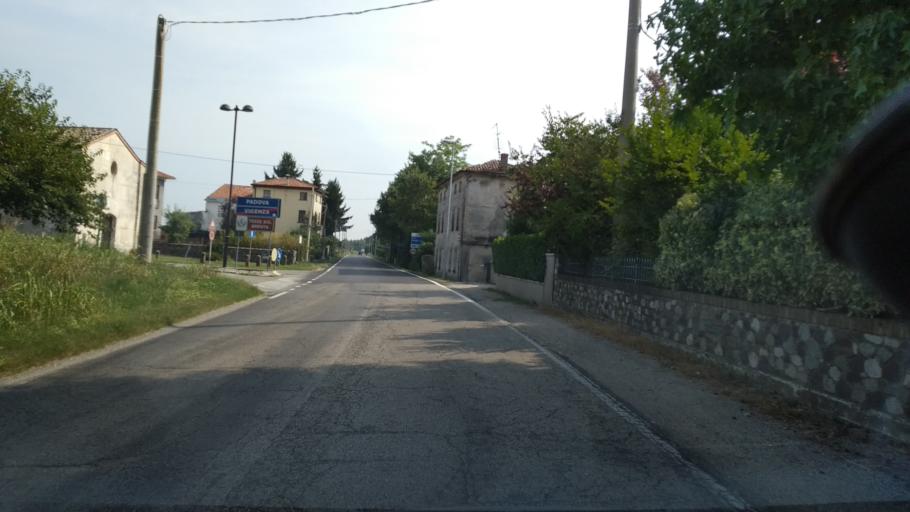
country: IT
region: Veneto
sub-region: Provincia di Vicenza
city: Tezze
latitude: 45.6808
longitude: 11.7066
